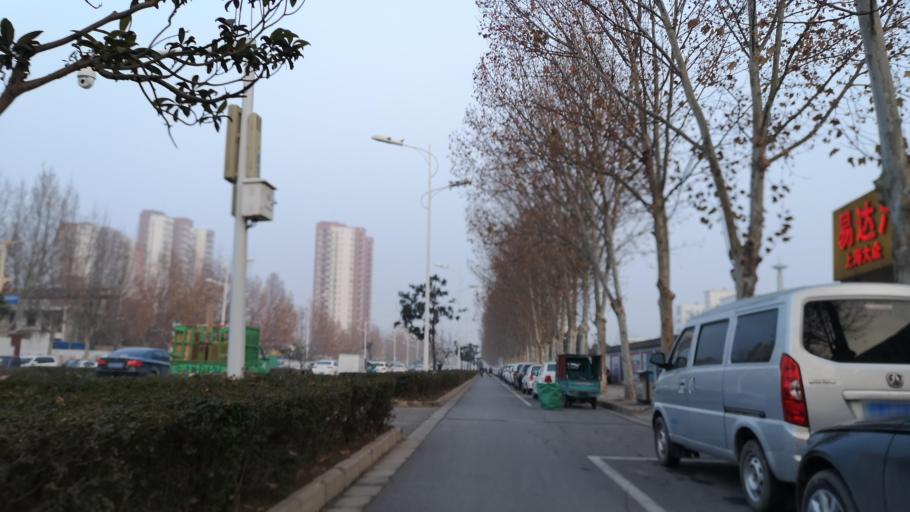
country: CN
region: Henan Sheng
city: Puyang
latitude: 35.7487
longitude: 115.0334
